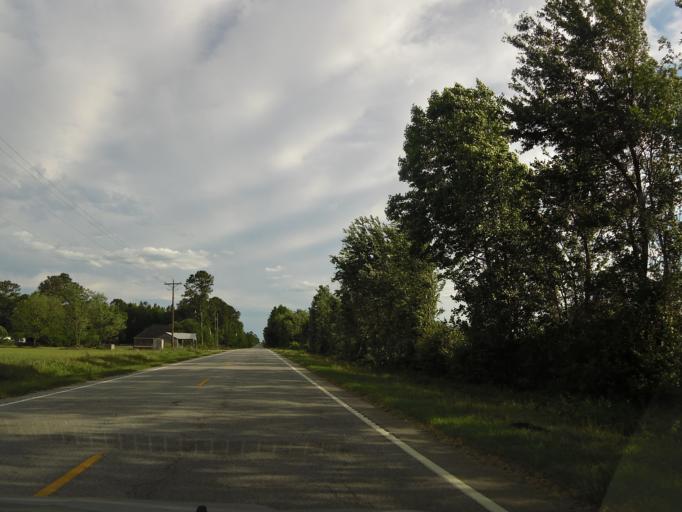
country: US
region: South Carolina
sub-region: Hampton County
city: Estill
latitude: 32.6623
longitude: -81.2435
